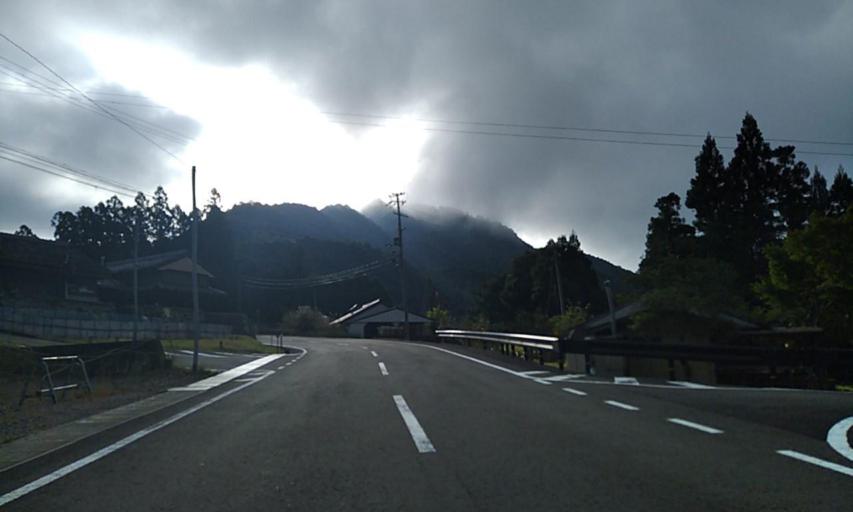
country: JP
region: Wakayama
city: Shingu
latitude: 33.8764
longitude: 135.8657
